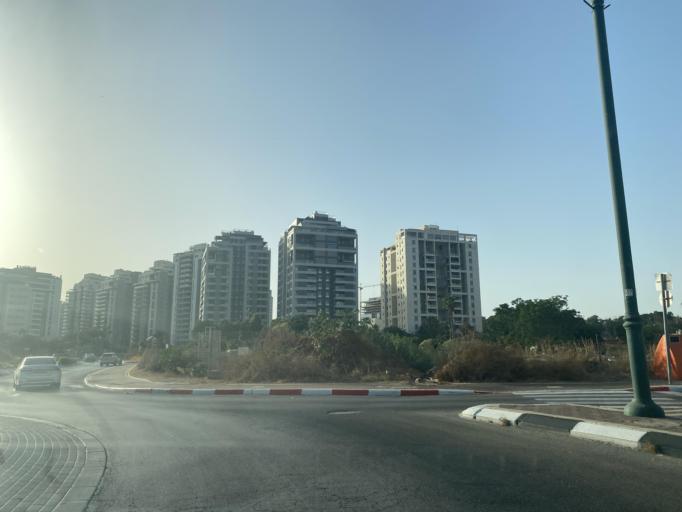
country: IL
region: Central District
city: Kfar Saba
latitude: 32.1637
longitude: 34.9078
